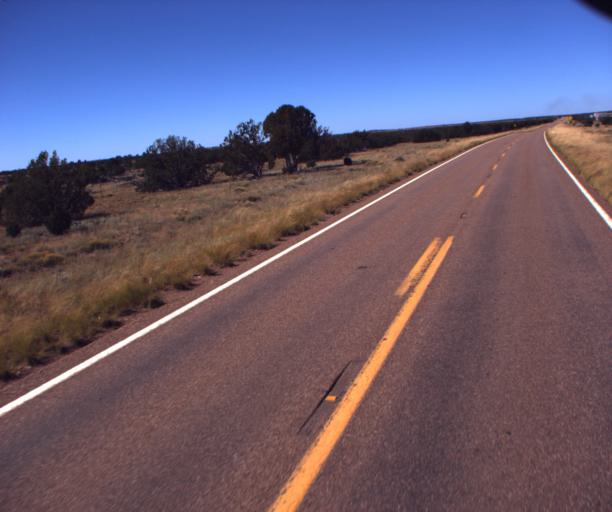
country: US
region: Arizona
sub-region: Navajo County
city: Heber-Overgaard
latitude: 34.4606
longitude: -110.3951
